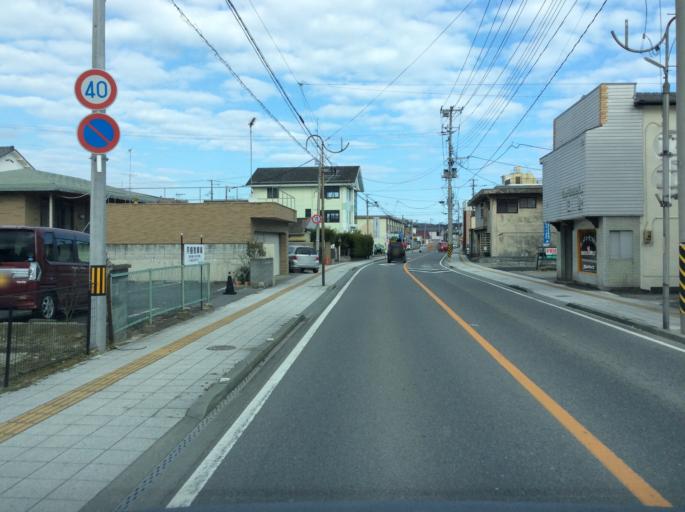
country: JP
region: Fukushima
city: Iwaki
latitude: 36.9505
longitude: 140.8933
